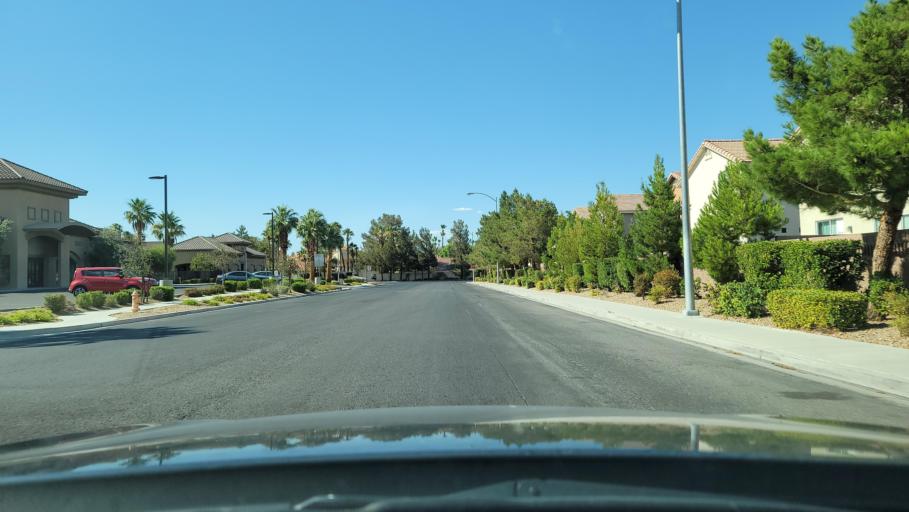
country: US
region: Nevada
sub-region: Clark County
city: Spring Valley
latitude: 36.0910
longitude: -115.2474
